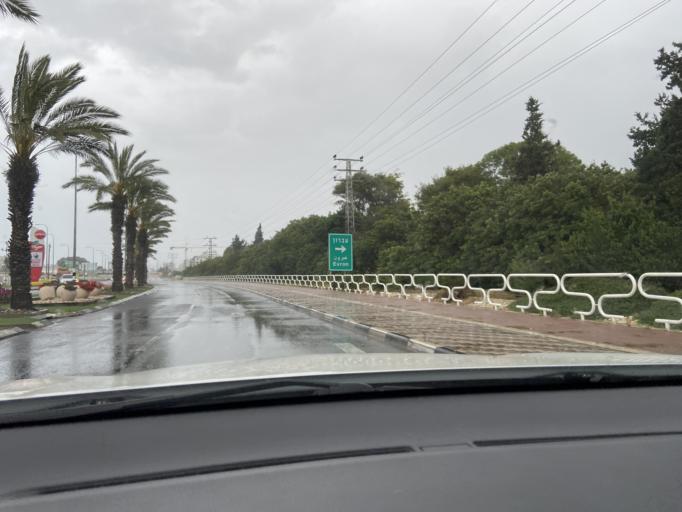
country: IL
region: Northern District
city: El Mazra`a
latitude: 32.9912
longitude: 35.0966
